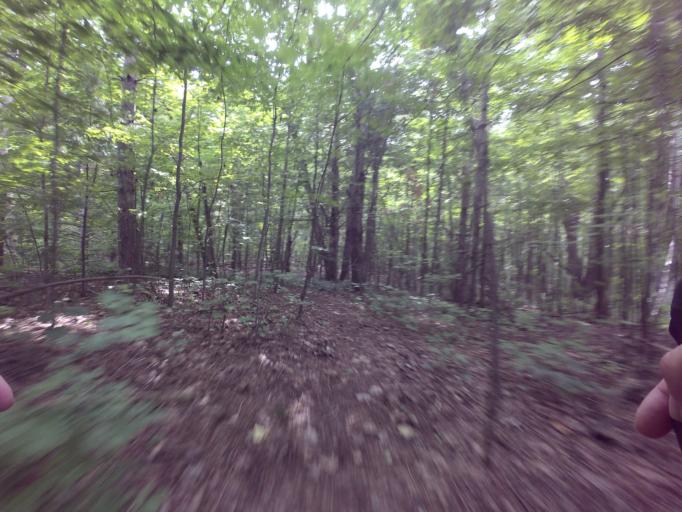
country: CA
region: Ontario
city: Bells Corners
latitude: 45.3214
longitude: -75.7912
